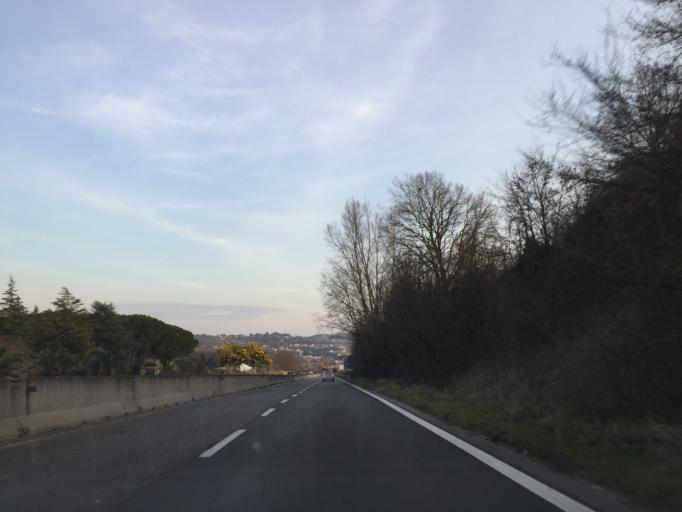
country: IT
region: Latium
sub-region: Citta metropolitana di Roma Capitale
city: Campagnano di Roma
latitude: 42.1336
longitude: 12.3548
